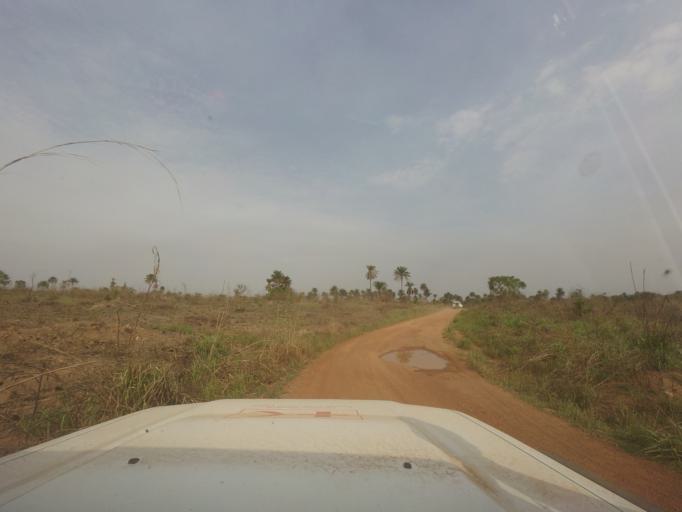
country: GN
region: Nzerekore
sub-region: Prefecture de Guekedou
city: Gueckedou
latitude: 8.5267
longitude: -10.2304
